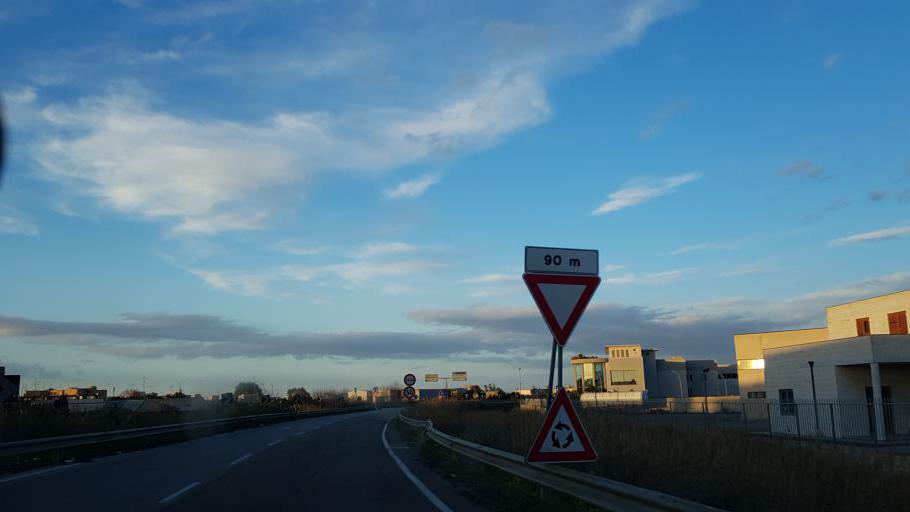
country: IT
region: Apulia
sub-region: Provincia di Brindisi
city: La Rosa
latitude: 40.6237
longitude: 17.9572
